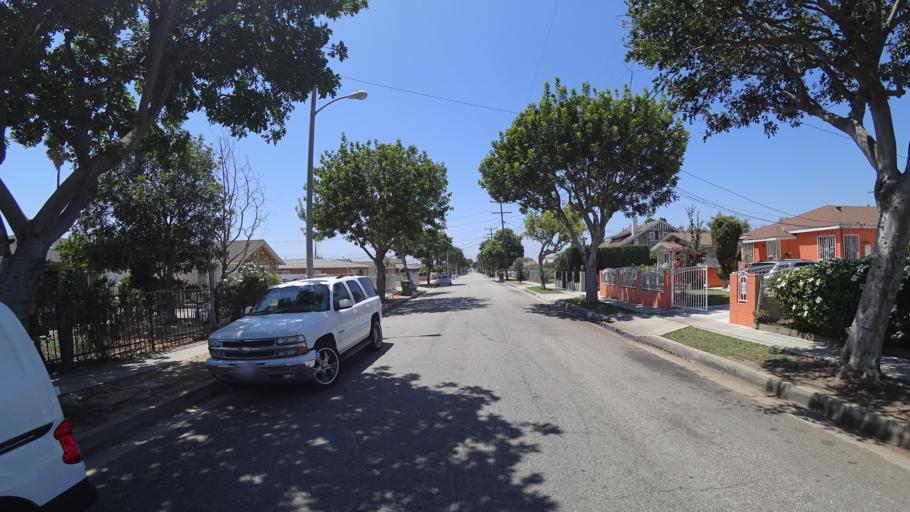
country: US
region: California
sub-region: Los Angeles County
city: Lennox
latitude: 33.9377
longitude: -118.3313
